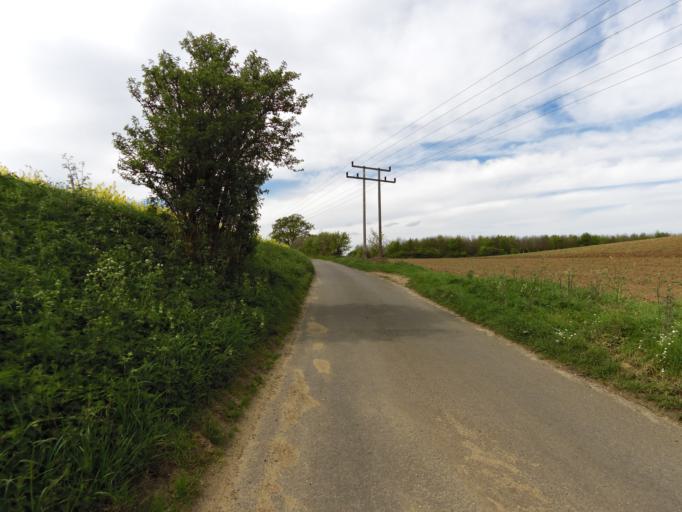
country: GB
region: England
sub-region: Essex
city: Mistley
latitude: 51.9967
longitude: 1.1249
